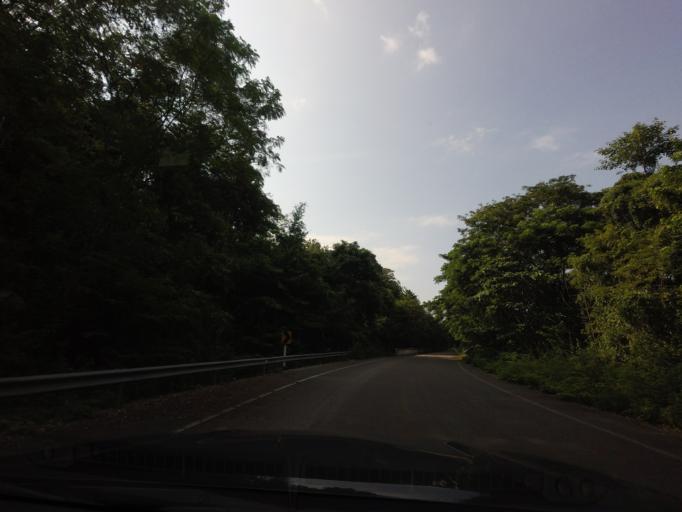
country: TH
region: Nan
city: Na Noi
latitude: 18.3418
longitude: 100.8832
